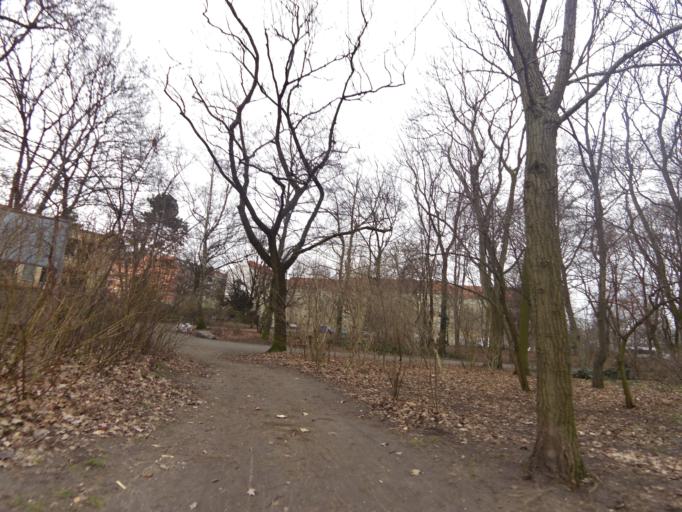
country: DE
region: Berlin
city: Tempelhof Bezirk
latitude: 52.4809
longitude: 13.4197
